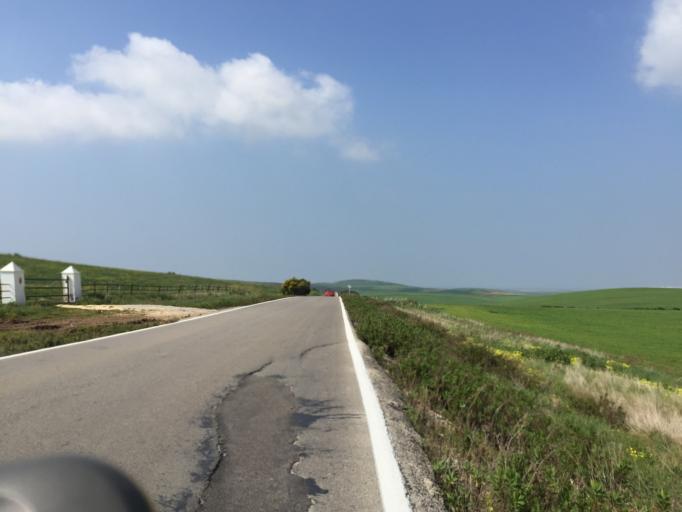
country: ES
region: Andalusia
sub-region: Provincia de Cadiz
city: Vejer de la Frontera
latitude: 36.2365
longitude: -6.0111
